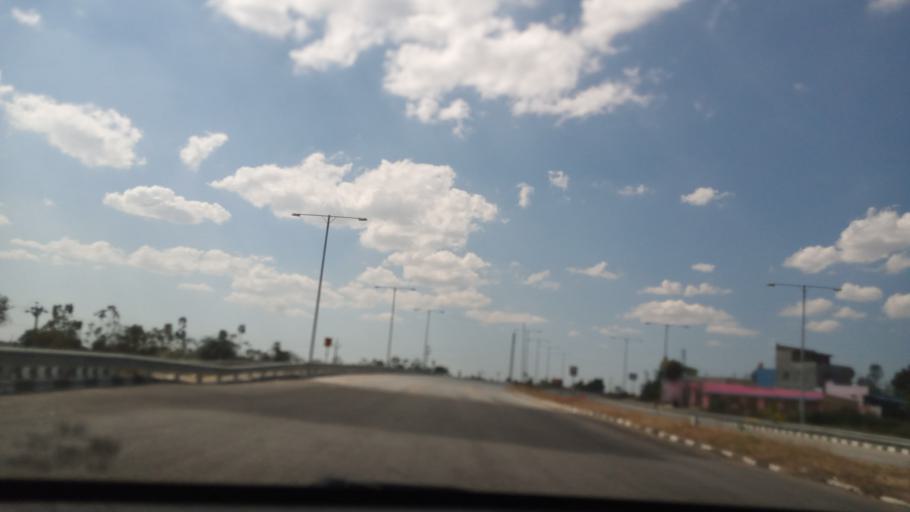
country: IN
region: Andhra Pradesh
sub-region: Chittoor
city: Palmaner
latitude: 13.2159
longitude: 78.7458
